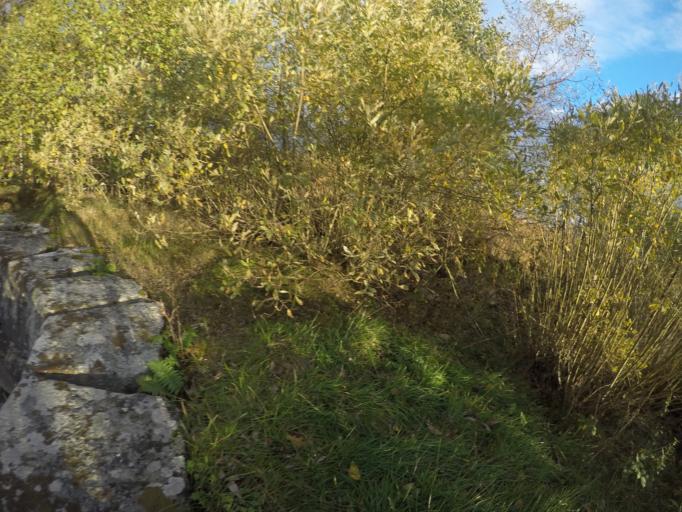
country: SE
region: Vaestmanland
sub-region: Arboga Kommun
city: Tyringe
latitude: 59.2910
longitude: 16.0029
